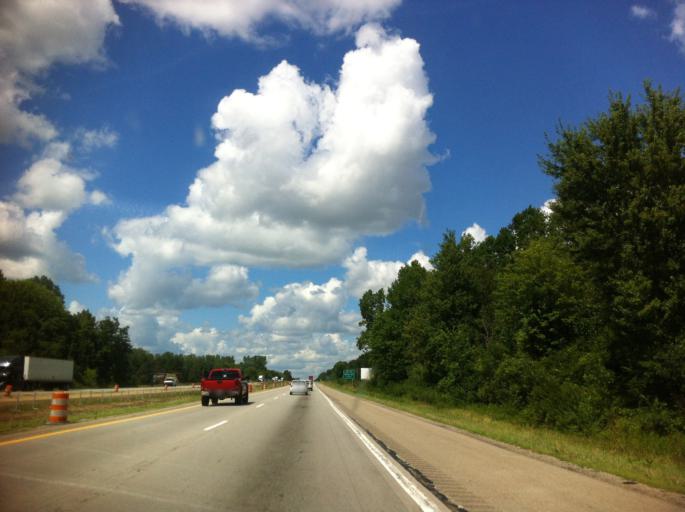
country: US
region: Michigan
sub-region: Washtenaw County
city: Milan
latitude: 42.1359
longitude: -83.6831
